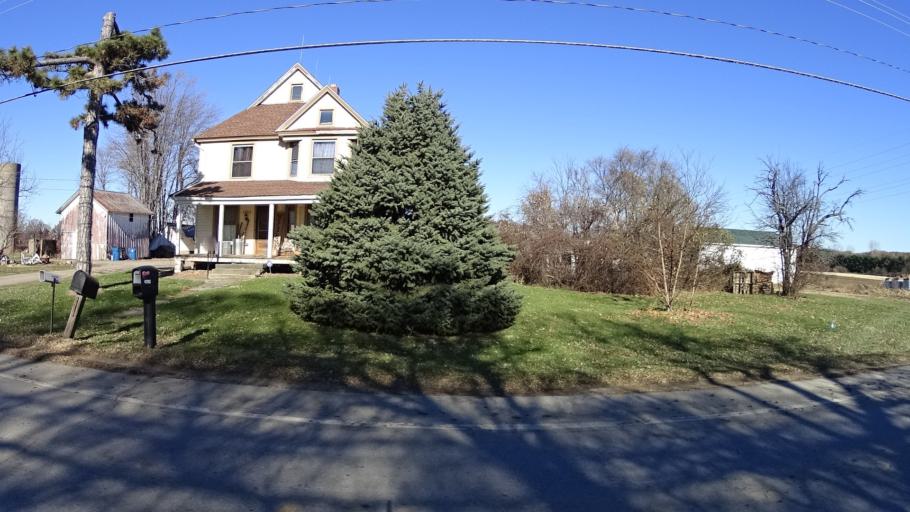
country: US
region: Ohio
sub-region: Lorain County
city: Elyria
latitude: 41.3753
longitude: -82.1566
